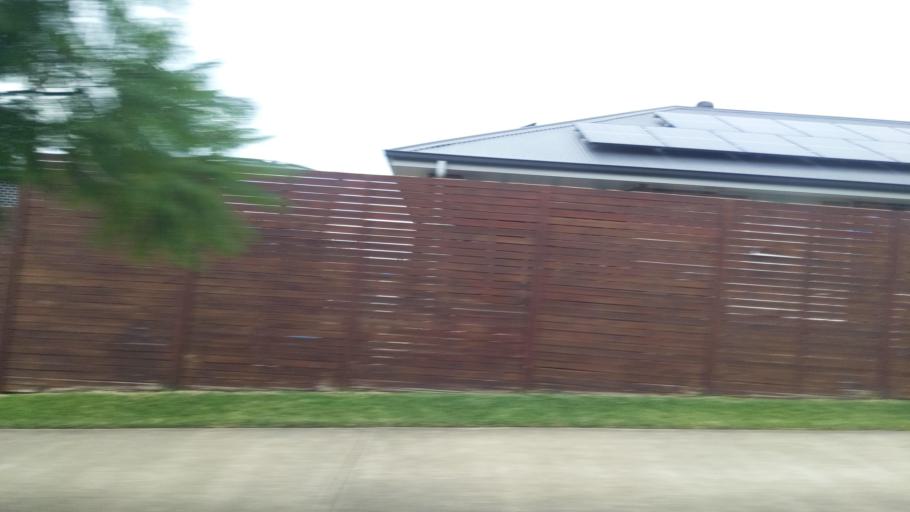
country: AU
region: New South Wales
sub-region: Blacktown
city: Quakers Hill
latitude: -33.7240
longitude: 150.8639
